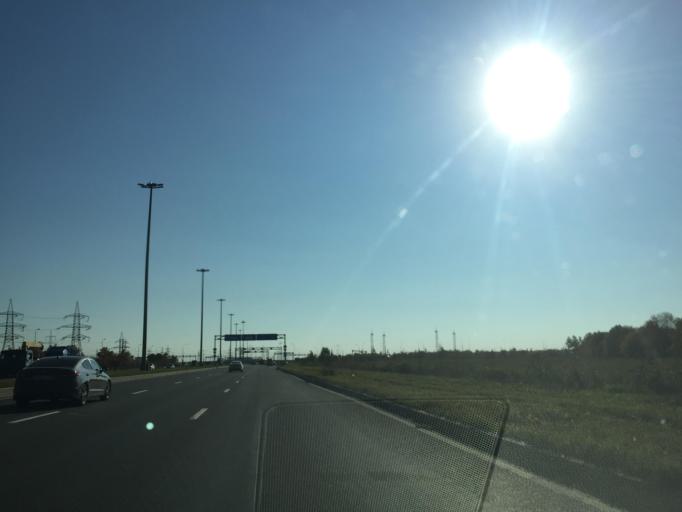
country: RU
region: St.-Petersburg
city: Metallostroy
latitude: 59.7515
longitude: 30.5262
